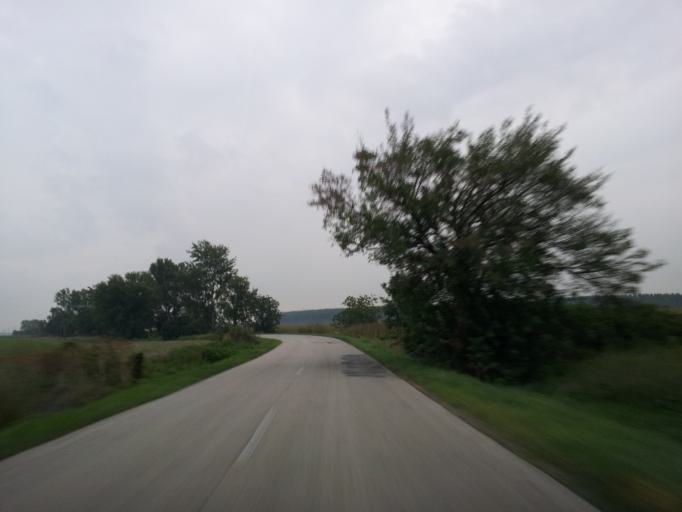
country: HU
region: Tolna
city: Fadd
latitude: 46.4868
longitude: 18.8393
